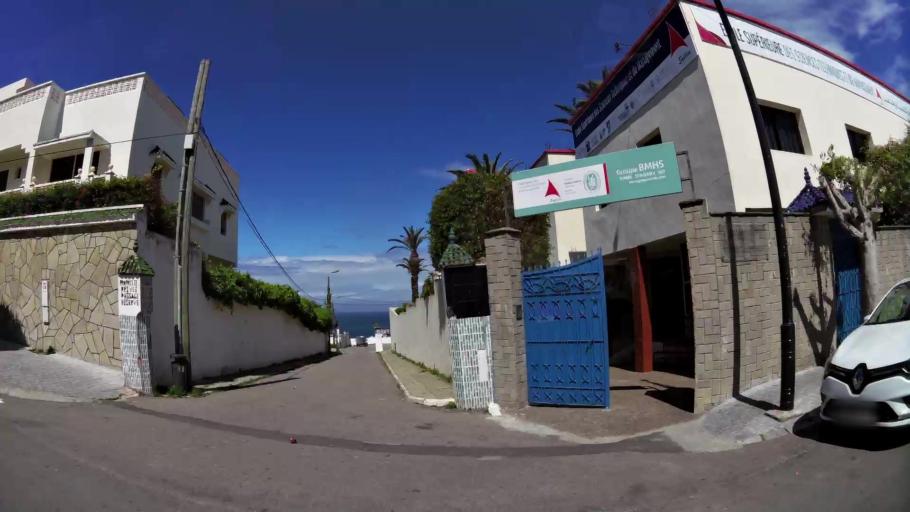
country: MA
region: Tanger-Tetouan
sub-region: Tanger-Assilah
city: Tangier
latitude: 35.7896
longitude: -5.8197
